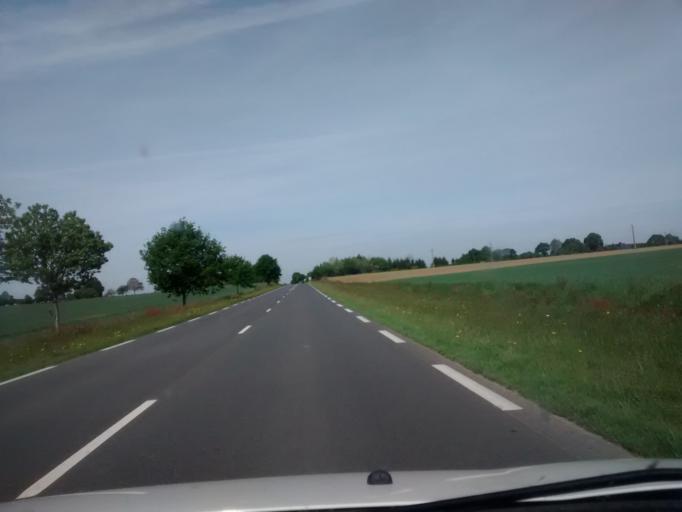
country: FR
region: Brittany
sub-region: Departement d'Ille-et-Vilaine
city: Saint-Brice-en-Cogles
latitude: 48.4224
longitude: -1.4166
